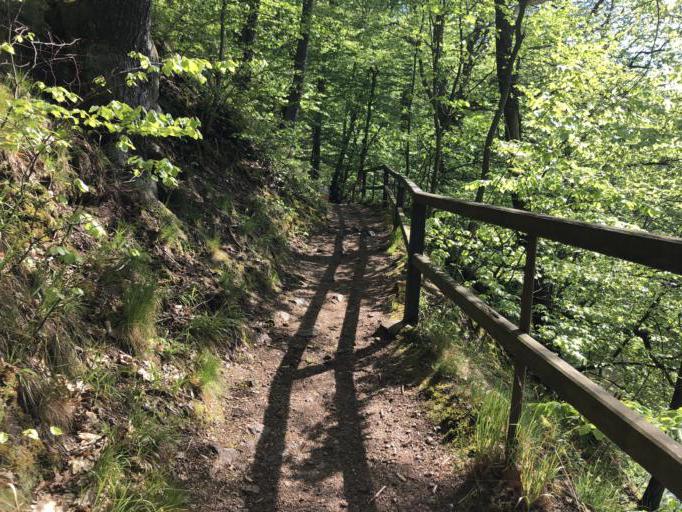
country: DE
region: Saxony
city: Wechselburg
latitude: 51.0089
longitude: 12.7838
